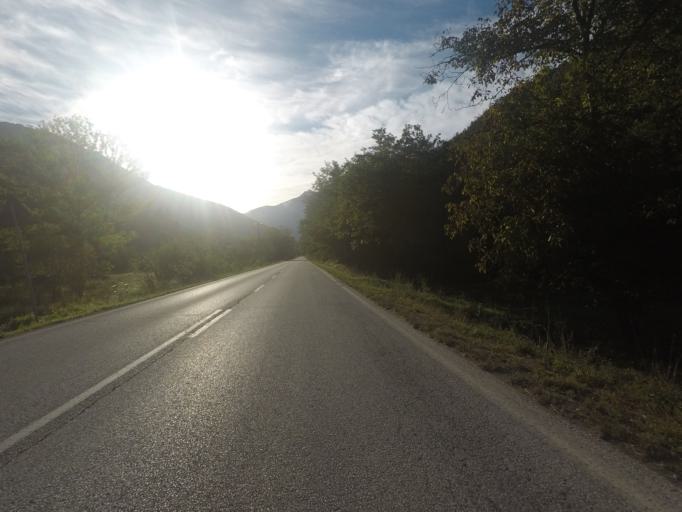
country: IT
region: Tuscany
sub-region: Provincia di Lucca
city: Valdottavo
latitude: 43.9699
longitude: 10.4891
